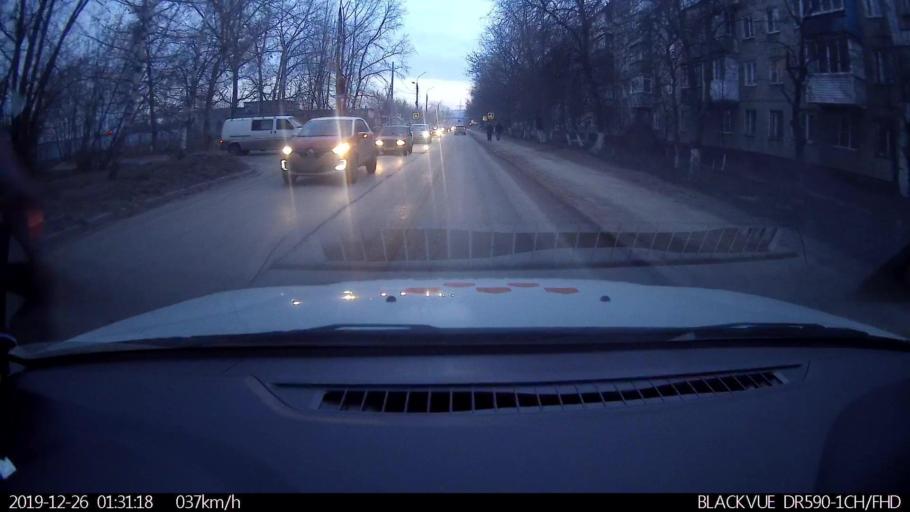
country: RU
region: Nizjnij Novgorod
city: Nizhniy Novgorod
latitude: 56.2685
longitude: 43.8978
